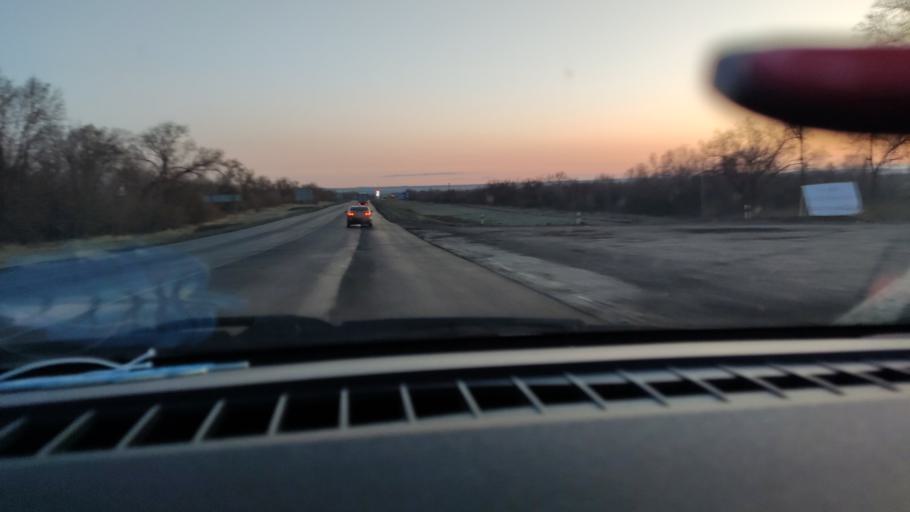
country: RU
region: Saratov
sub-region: Saratovskiy Rayon
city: Saratov
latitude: 51.6754
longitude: 46.0008
